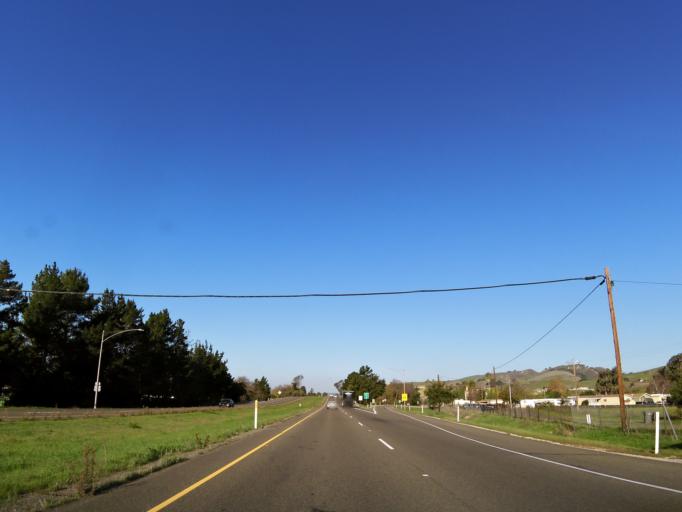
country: US
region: California
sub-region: Santa Barbara County
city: Los Alamos
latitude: 34.7401
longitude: -120.2674
